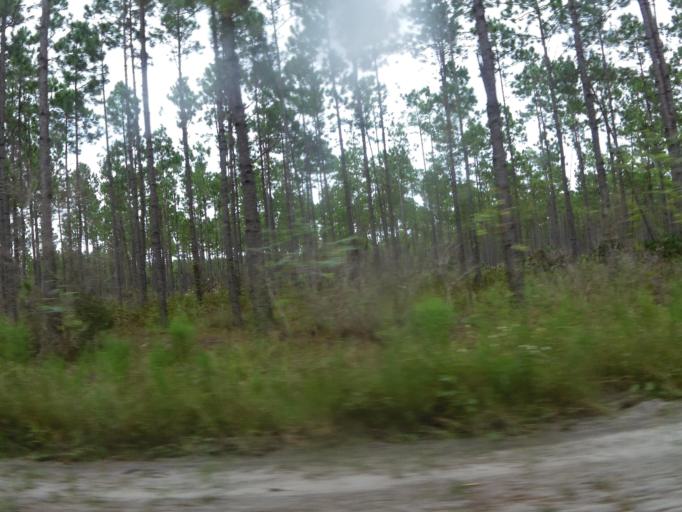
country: US
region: Florida
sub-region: Flagler County
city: Palm Coast
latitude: 29.5943
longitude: -81.3537
